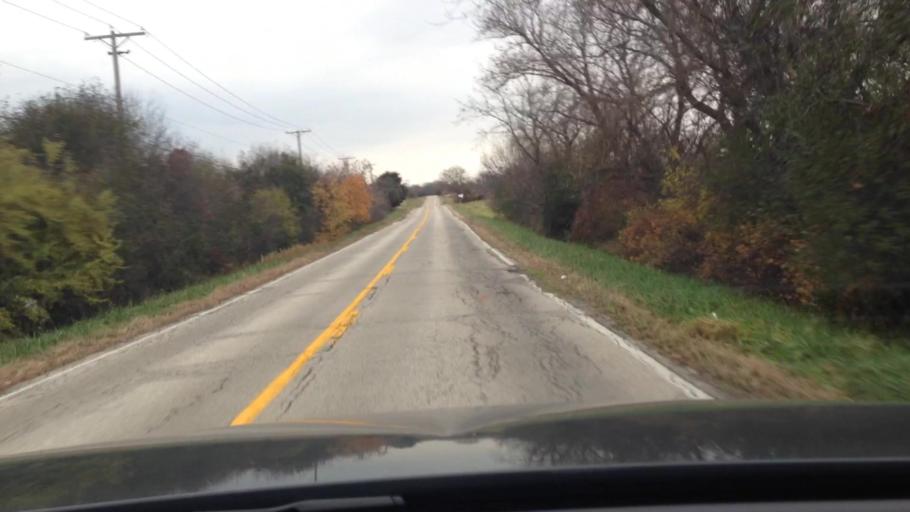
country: US
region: Illinois
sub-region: McHenry County
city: Woodstock
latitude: 42.2739
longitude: -88.4496
